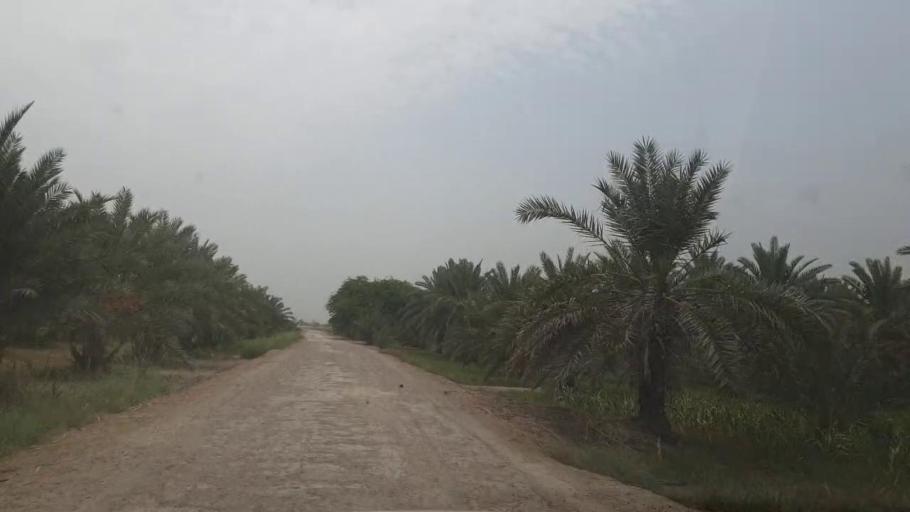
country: PK
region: Sindh
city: Kot Diji
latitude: 27.4330
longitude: 68.6286
